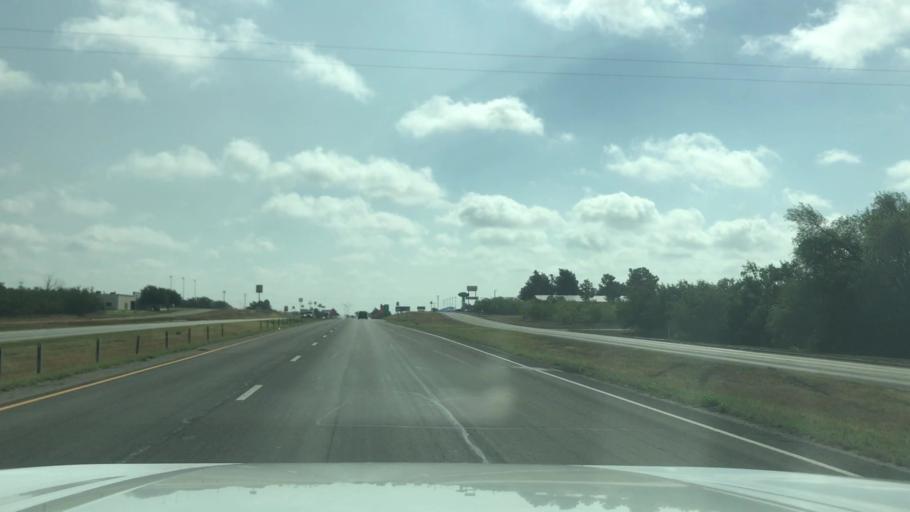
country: US
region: Texas
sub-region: Nolan County
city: Sweetwater
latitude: 32.4478
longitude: -100.4098
